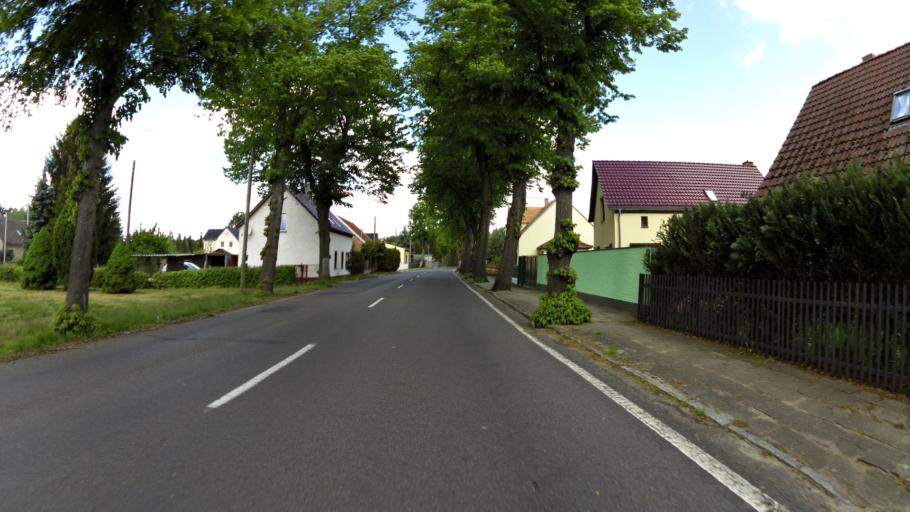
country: DE
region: Brandenburg
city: Schlepzig
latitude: 52.1221
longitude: 13.9496
